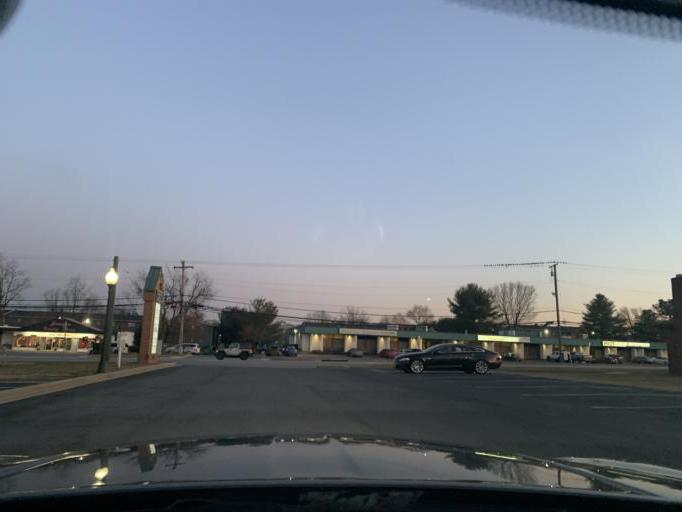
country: US
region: Maryland
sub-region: Anne Arundel County
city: Glen Burnie
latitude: 39.1483
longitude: -76.6396
